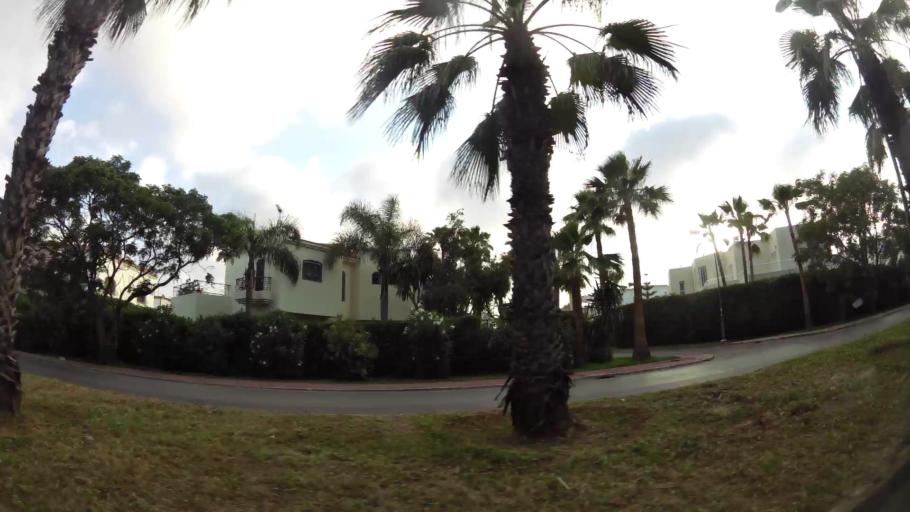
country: MA
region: Rabat-Sale-Zemmour-Zaer
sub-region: Rabat
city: Rabat
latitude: 33.9589
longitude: -6.8512
